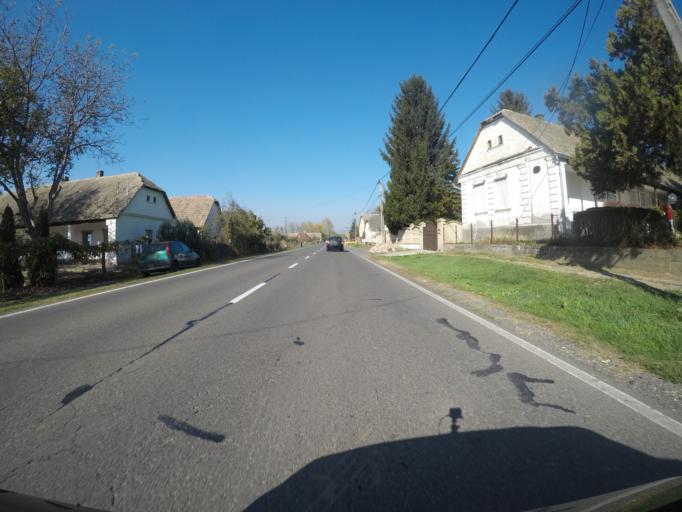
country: HU
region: Tolna
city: Szedres
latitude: 46.5103
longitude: 18.6658
